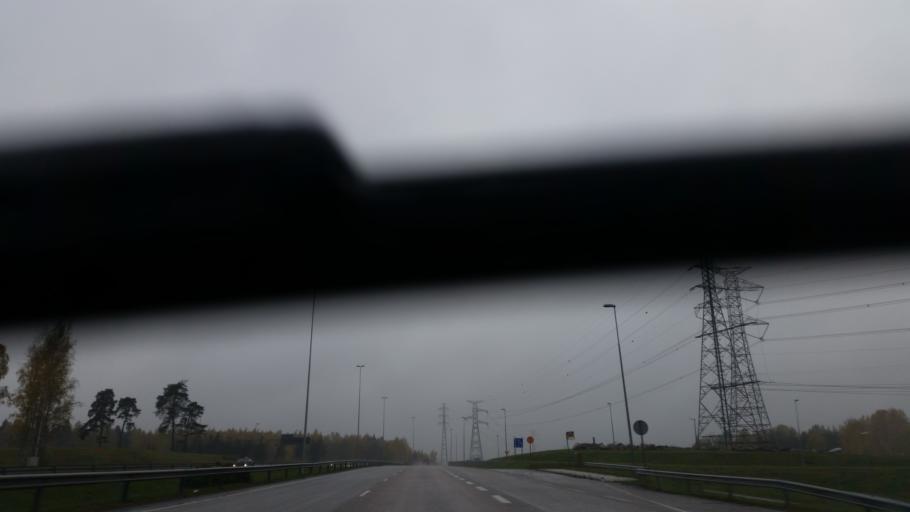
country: FI
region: Uusimaa
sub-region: Helsinki
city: Teekkarikylae
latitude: 60.2942
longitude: 24.8612
